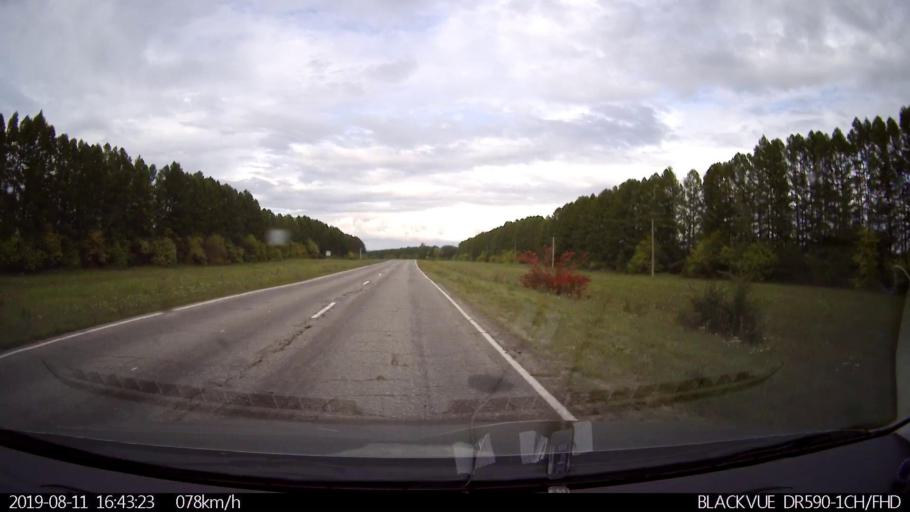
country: RU
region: Ulyanovsk
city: Mayna
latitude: 54.1684
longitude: 47.6714
